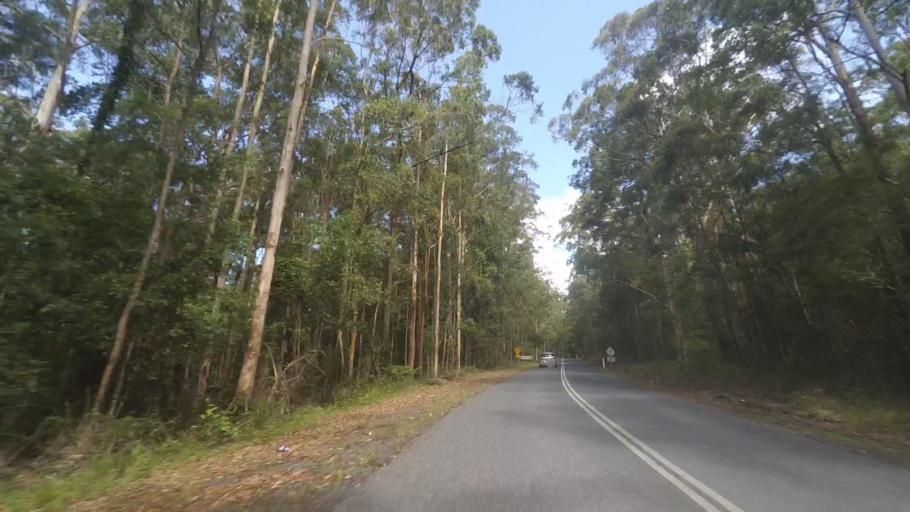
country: AU
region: New South Wales
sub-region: Great Lakes
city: Bulahdelah
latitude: -32.3994
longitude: 152.2929
